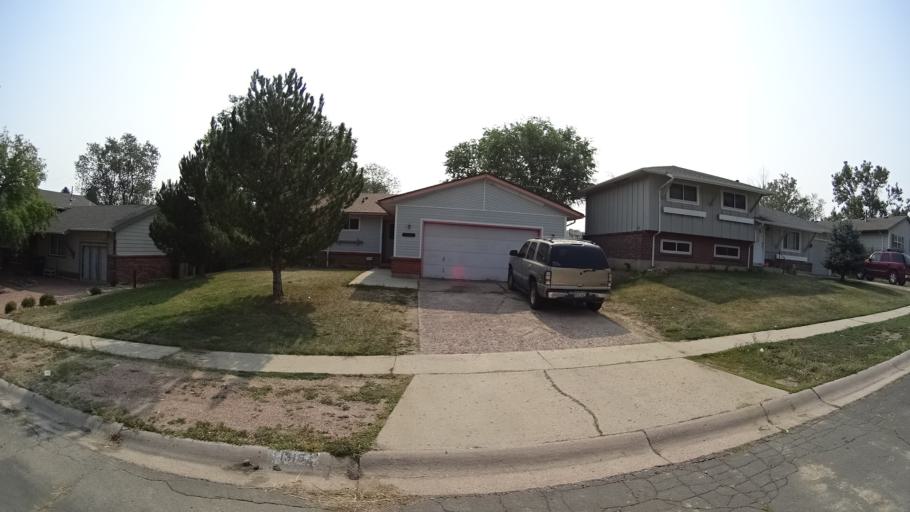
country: US
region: Colorado
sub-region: El Paso County
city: Stratmoor
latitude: 38.8124
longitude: -104.7735
